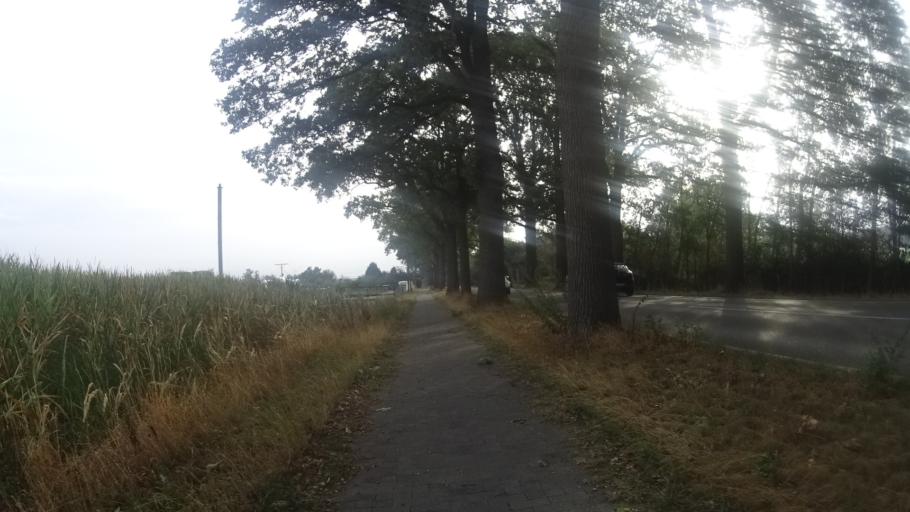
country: DE
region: North Rhine-Westphalia
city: Geldern
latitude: 51.5037
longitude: 6.2669
